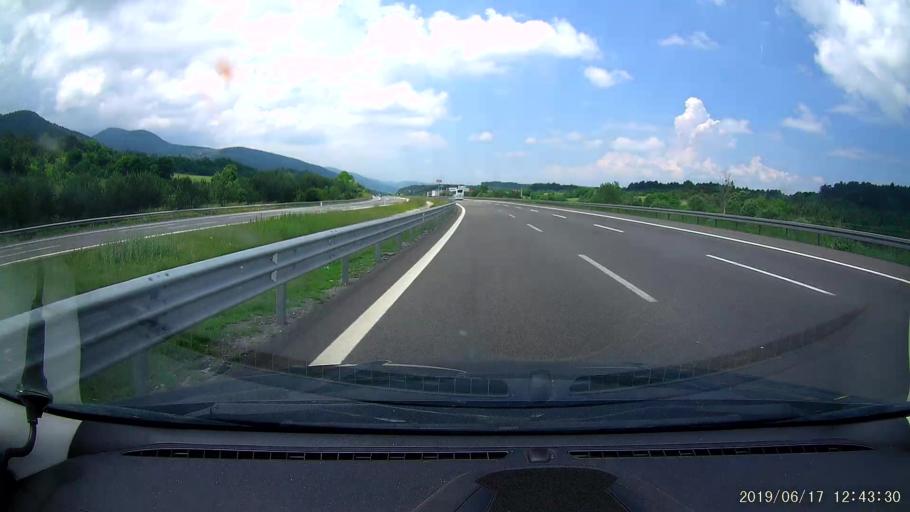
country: TR
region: Bolu
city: Yenicaga
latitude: 40.7548
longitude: 31.9152
